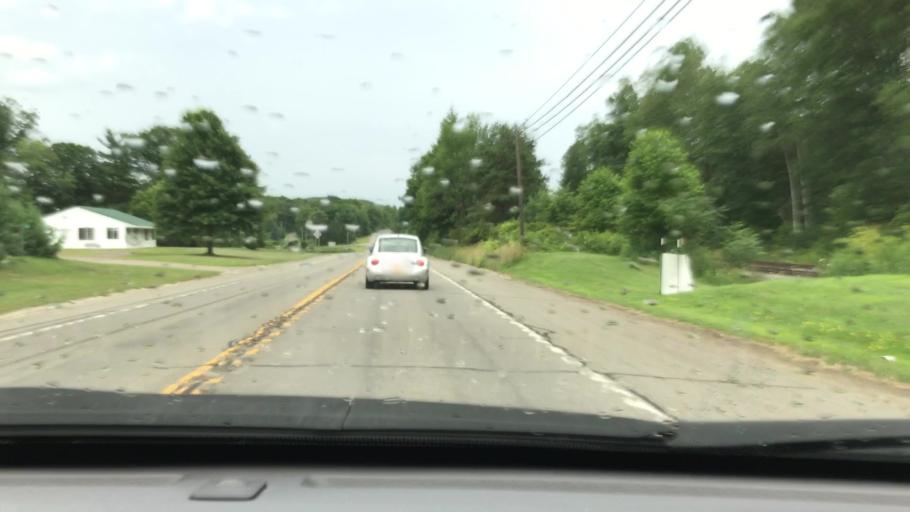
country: US
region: New York
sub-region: Cattaraugus County
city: Salamanca
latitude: 42.1839
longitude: -78.6828
